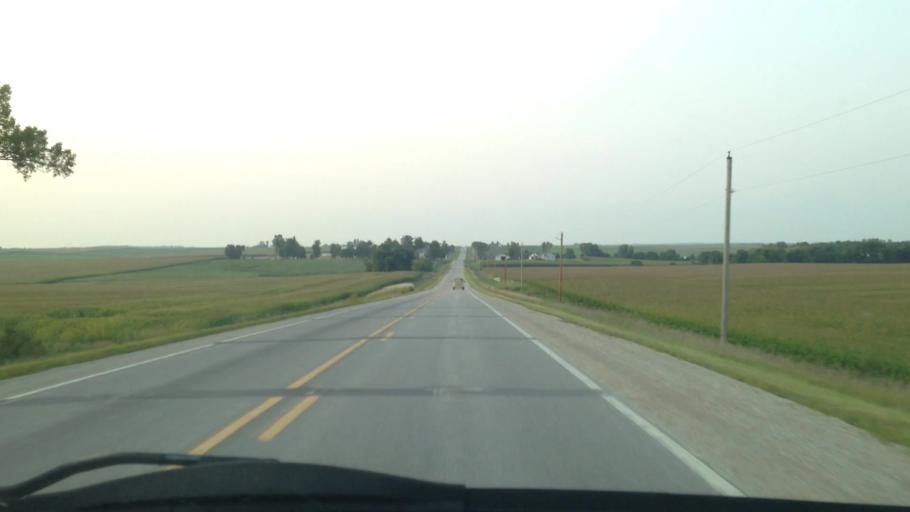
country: US
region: Iowa
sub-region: Benton County
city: Atkins
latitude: 41.9989
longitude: -91.8734
